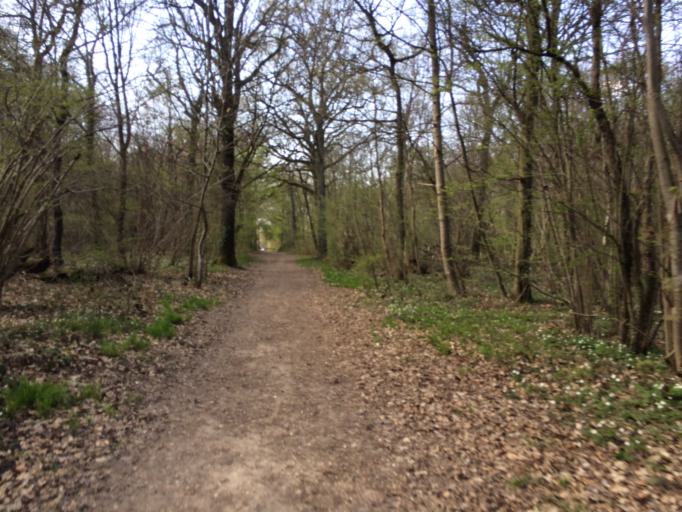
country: FR
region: Ile-de-France
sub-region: Departement de l'Essonne
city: Draveil
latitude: 48.6727
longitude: 2.4203
